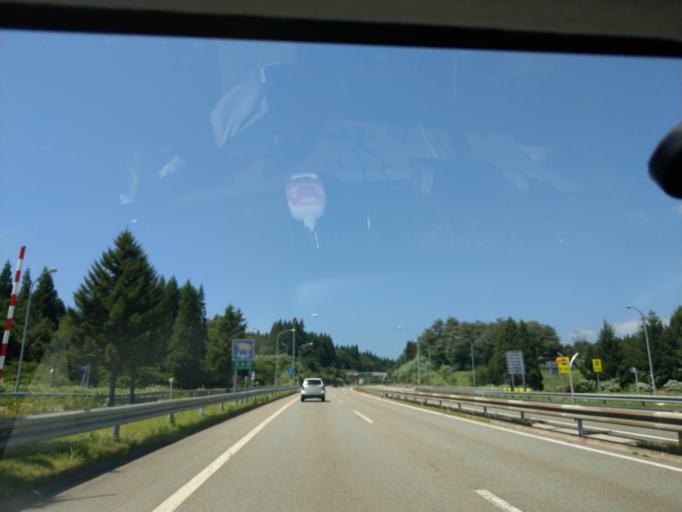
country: JP
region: Akita
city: Omagari
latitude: 39.4089
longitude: 140.4441
